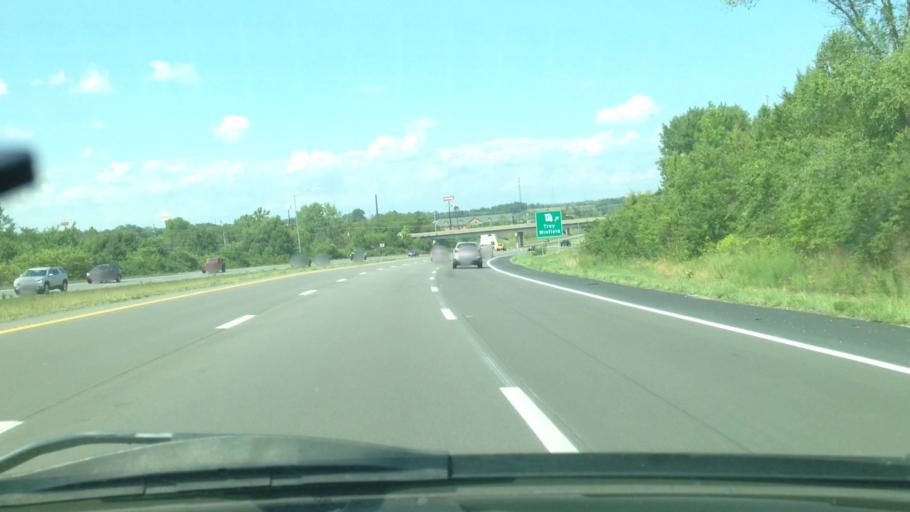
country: US
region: Missouri
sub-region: Lincoln County
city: Troy
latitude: 38.9809
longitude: -90.9649
